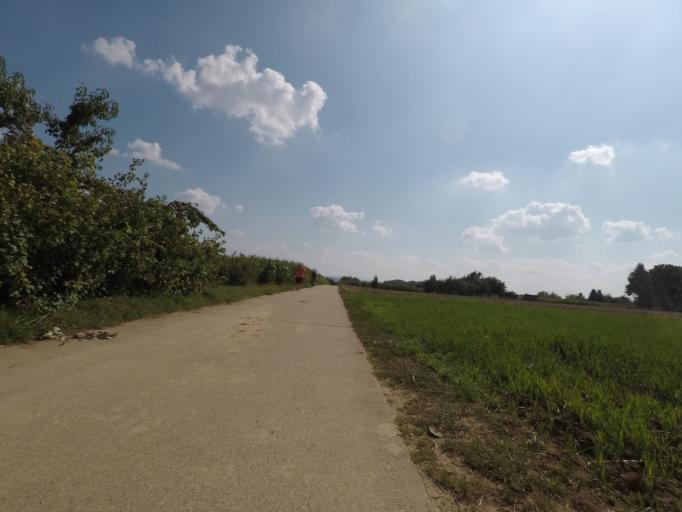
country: DE
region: Baden-Wuerttemberg
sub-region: Regierungsbezirk Stuttgart
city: Ostfildern
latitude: 48.7247
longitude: 9.2597
